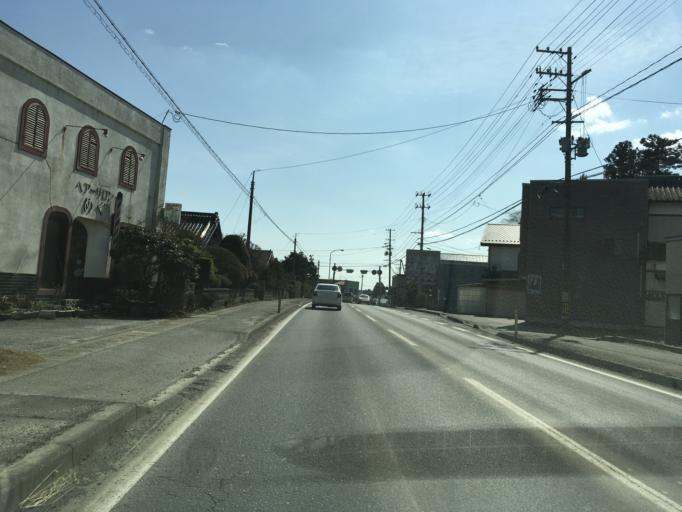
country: JP
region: Iwate
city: Ofunato
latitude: 38.8624
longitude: 141.5802
